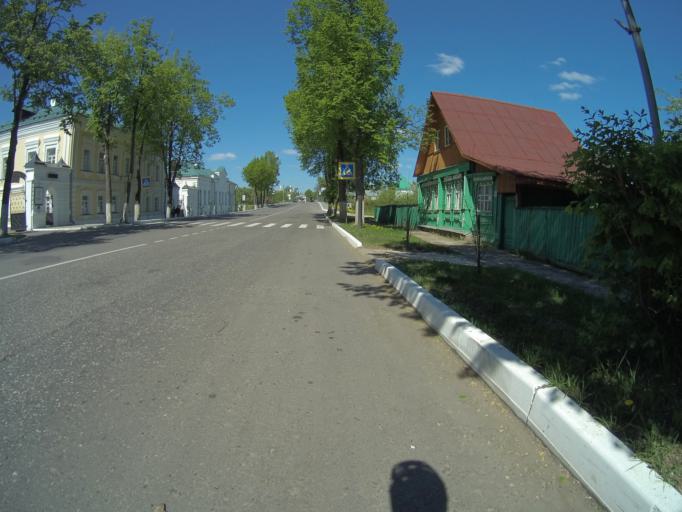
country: RU
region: Vladimir
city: Suzdal'
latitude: 56.4123
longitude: 40.4475
